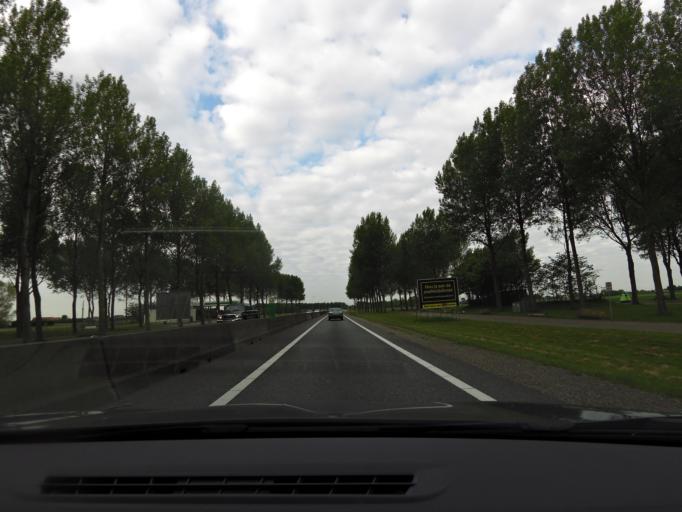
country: NL
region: South Holland
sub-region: Gemeente Brielle
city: Brielle
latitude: 51.8708
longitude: 4.1821
